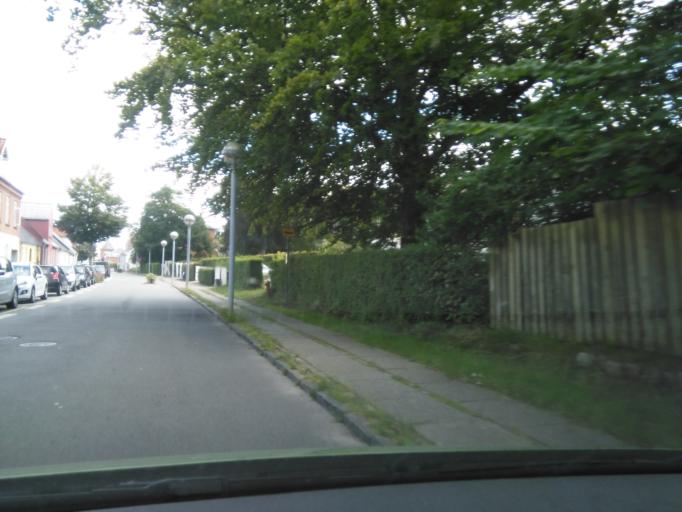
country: DK
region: Central Jutland
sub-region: Odder Kommune
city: Odder
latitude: 55.9687
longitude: 10.1375
